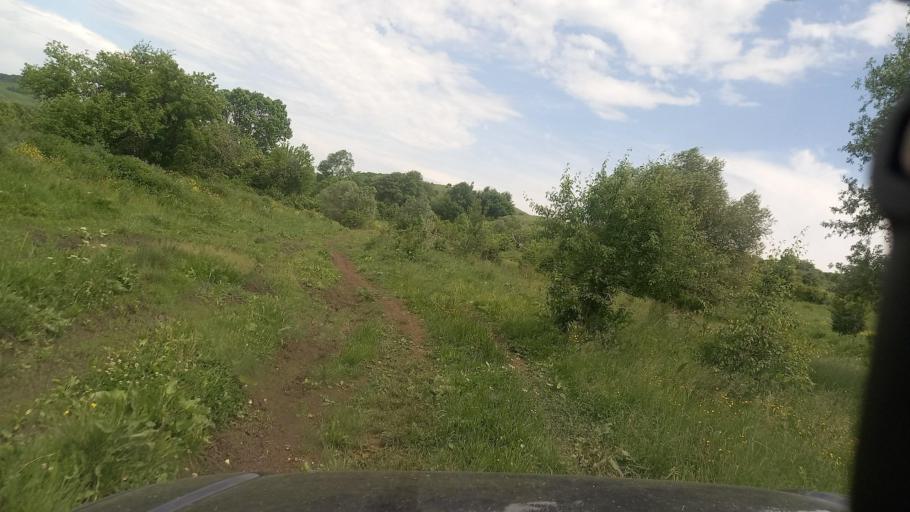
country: RU
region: Karachayevo-Cherkesiya
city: Pregradnaya
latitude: 44.0773
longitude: 41.2593
